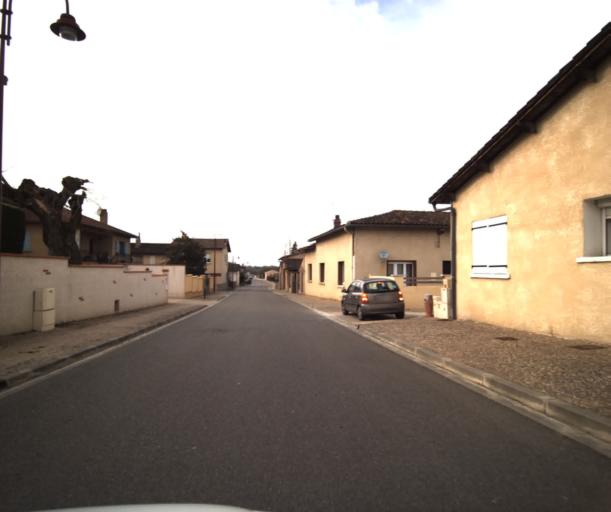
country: FR
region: Midi-Pyrenees
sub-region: Departement du Tarn-et-Garonne
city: Campsas
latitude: 43.8976
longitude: 1.3247
